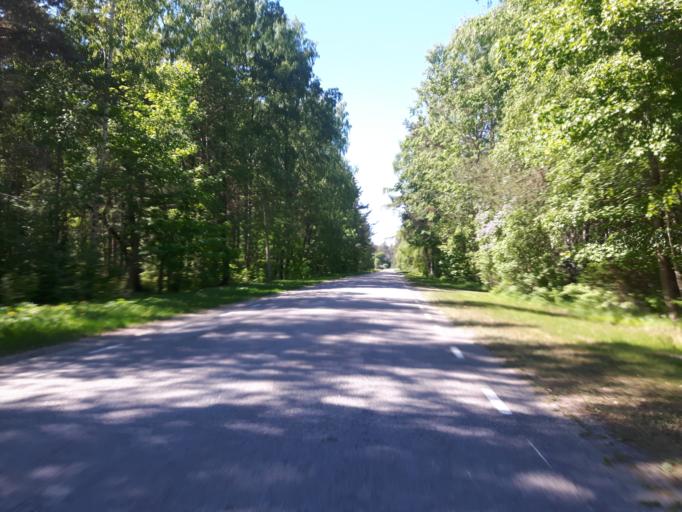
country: EE
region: Laeaene-Virumaa
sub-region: Viru-Nigula vald
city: Kunda
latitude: 59.4946
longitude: 26.4991
